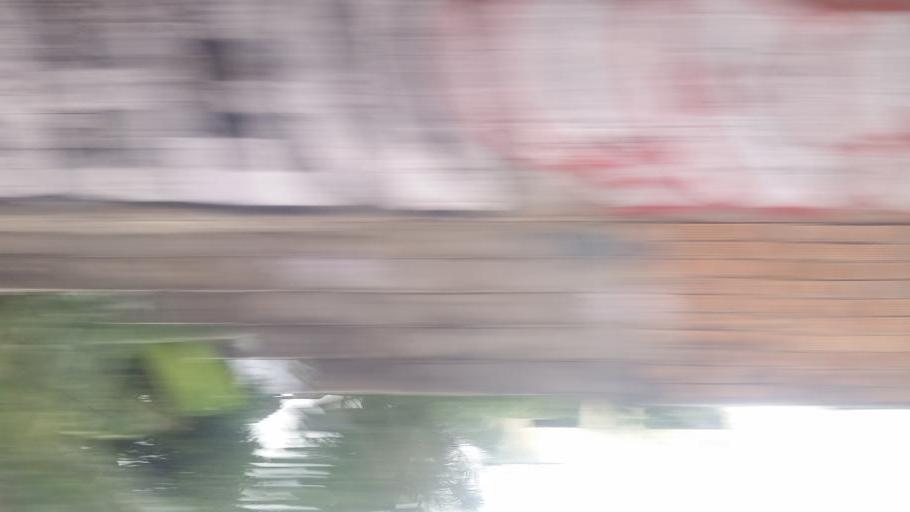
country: BR
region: Rio de Janeiro
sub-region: Rio De Janeiro
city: Rio de Janeiro
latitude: -22.8941
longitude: -43.3043
